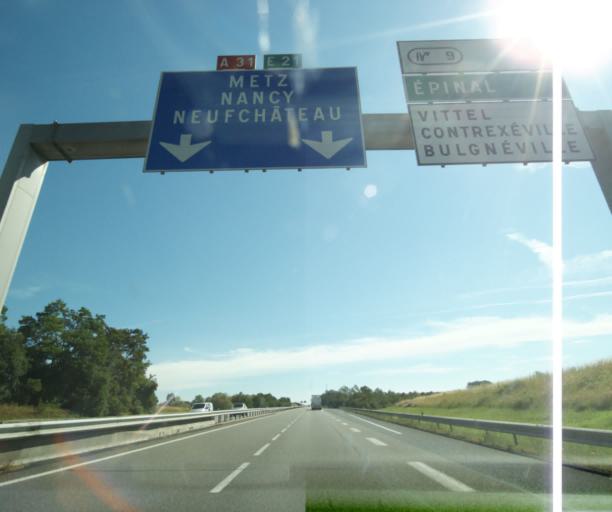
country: FR
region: Lorraine
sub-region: Departement des Vosges
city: Bulgneville
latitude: 48.2185
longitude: 5.8322
